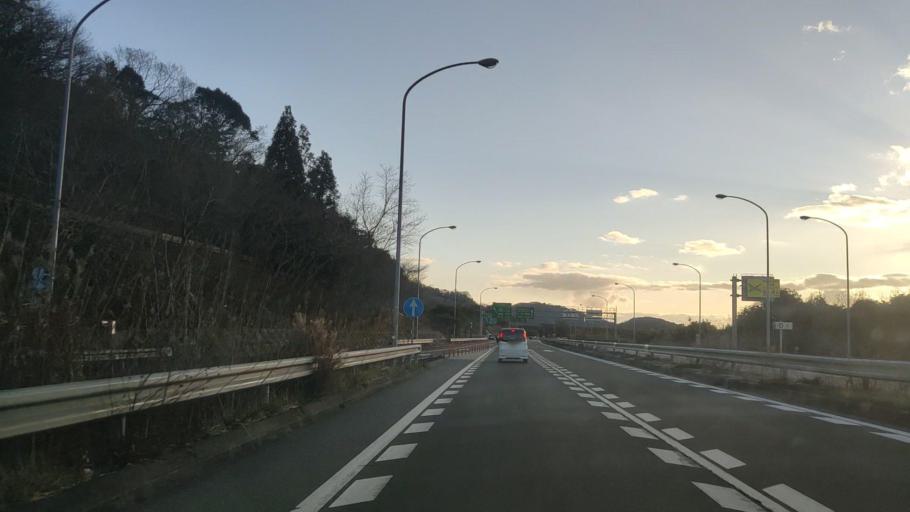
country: JP
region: Hyogo
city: Tatsunocho-tominaga
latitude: 34.8503
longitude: 134.6045
